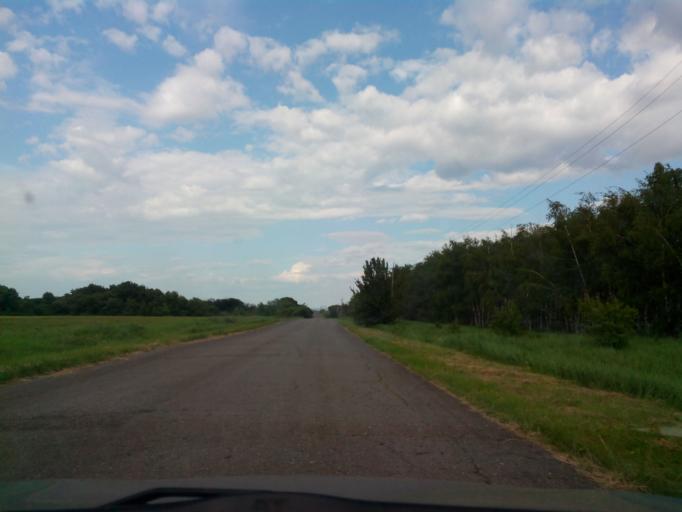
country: RU
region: Volgograd
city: Slashchevskaya
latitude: 49.7948
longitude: 42.3941
